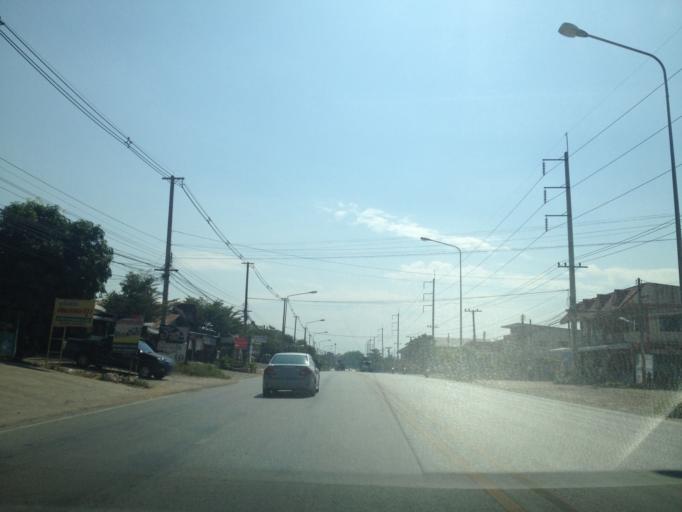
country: TH
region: Chiang Mai
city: Chom Thong
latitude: 18.4020
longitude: 98.6771
